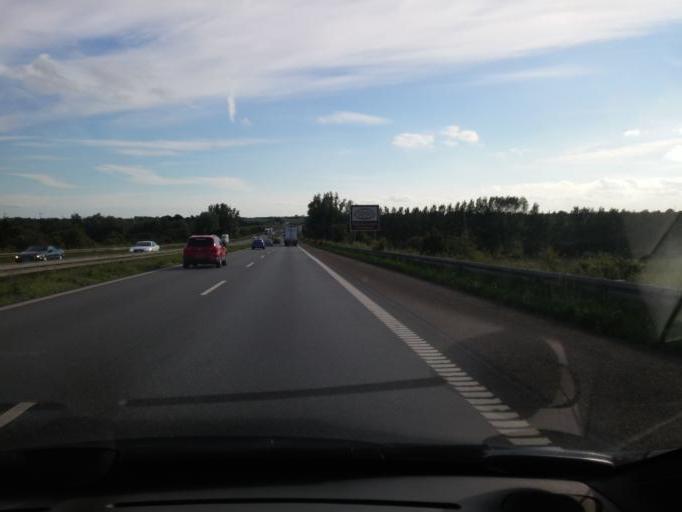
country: DK
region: Zealand
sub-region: Slagelse Kommune
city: Forlev
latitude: 55.3735
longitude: 11.3028
